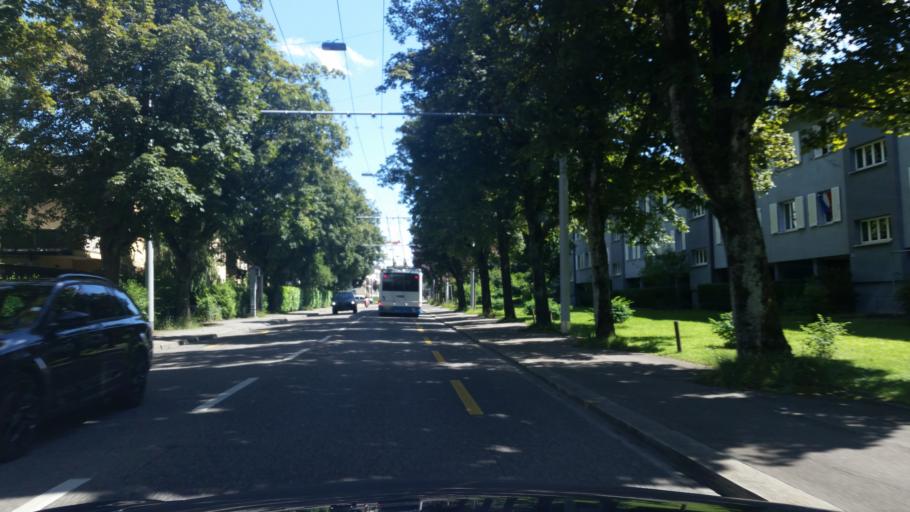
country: CH
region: Zurich
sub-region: Bezirk Zuerich
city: Zuerich (Kreis 11) / Oerlikon
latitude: 47.4087
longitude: 8.5294
